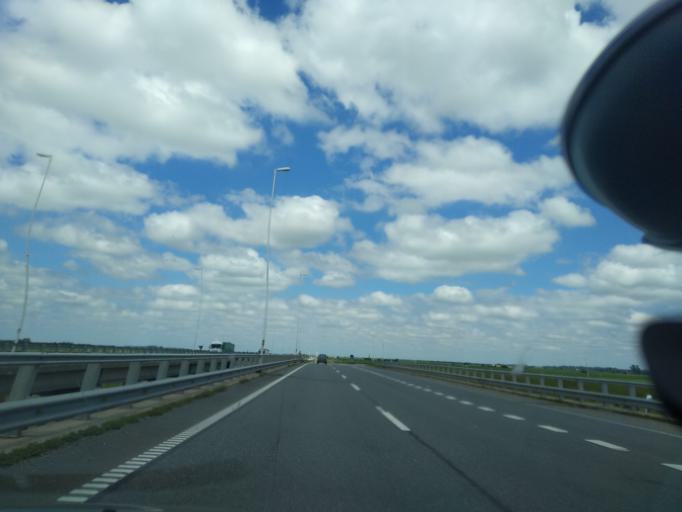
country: AR
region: Cordoba
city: Villa Maria
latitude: -32.4193
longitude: -63.1584
